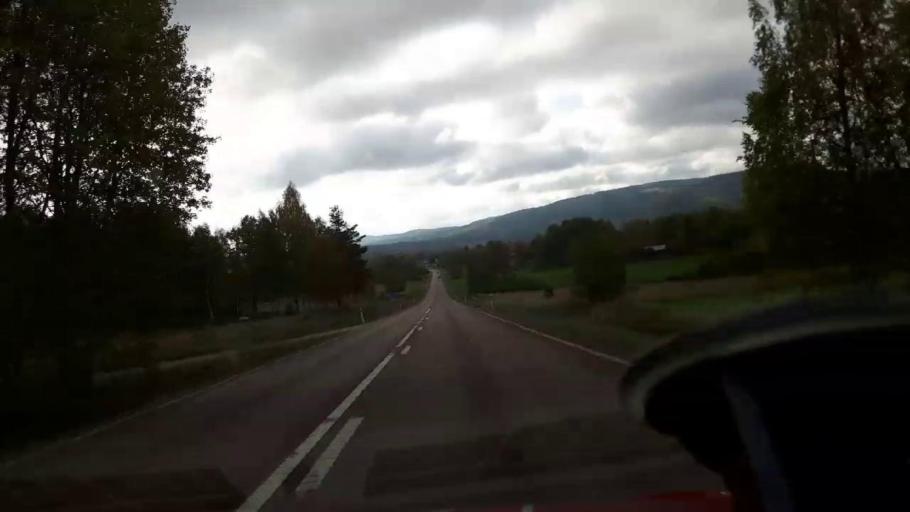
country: SE
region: Gaevleborg
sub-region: Ljusdals Kommun
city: Jaervsoe
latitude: 61.6824
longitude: 16.1457
